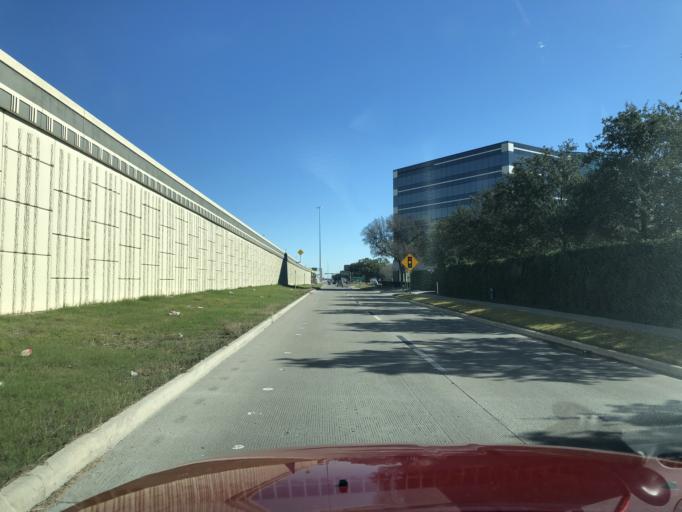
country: US
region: Texas
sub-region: Harris County
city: Hudson
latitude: 29.8503
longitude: -95.5089
